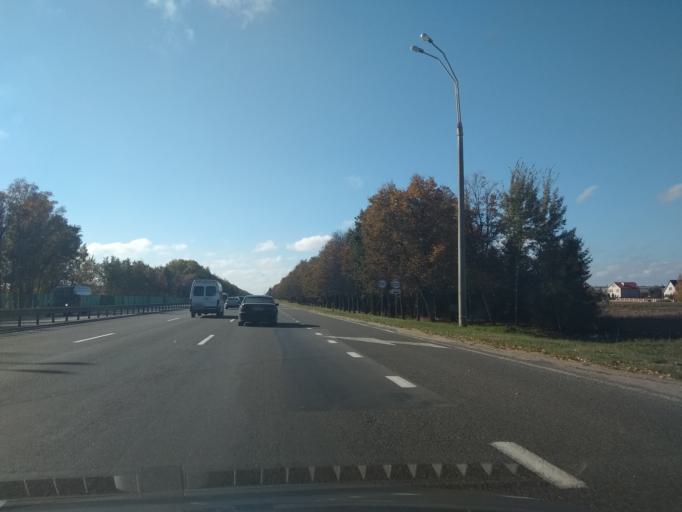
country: BY
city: Fanipol
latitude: 53.7595
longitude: 27.3352
